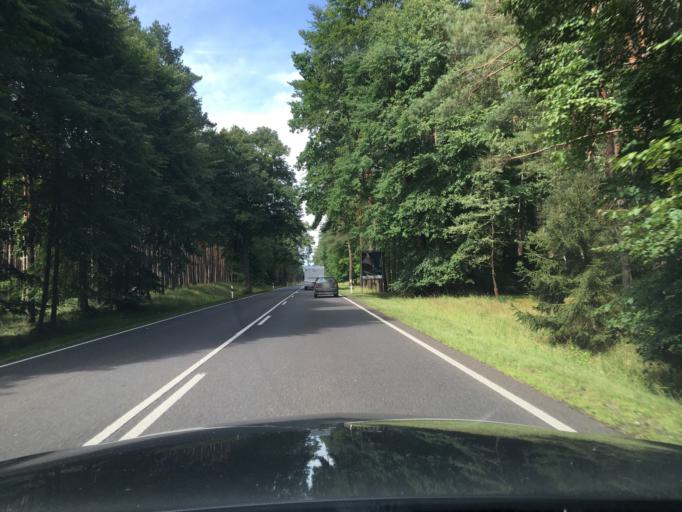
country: DE
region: Brandenburg
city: Furstenberg
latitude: 53.2664
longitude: 13.1156
